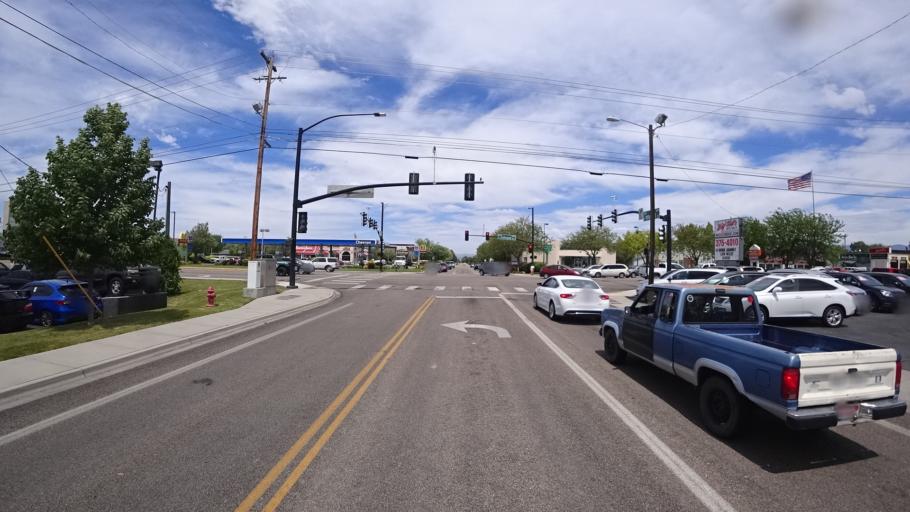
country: US
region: Idaho
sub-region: Ada County
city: Garden City
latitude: 43.6191
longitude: -116.3042
